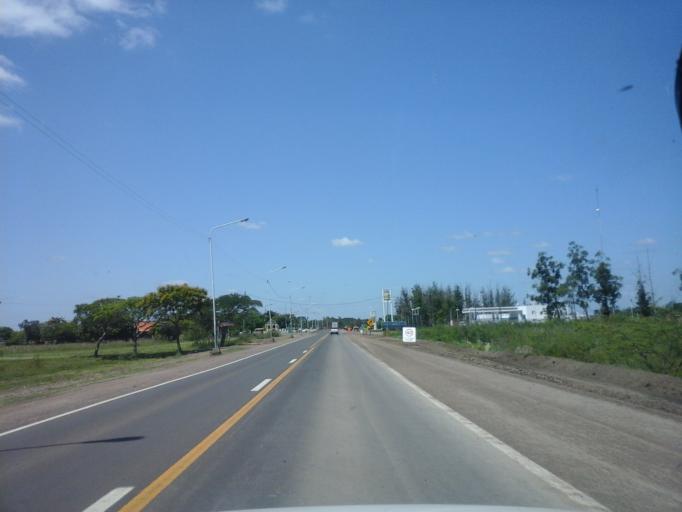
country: AR
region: Corrientes
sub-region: Departamento de Itati
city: Itati
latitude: -27.3487
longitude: -58.2338
